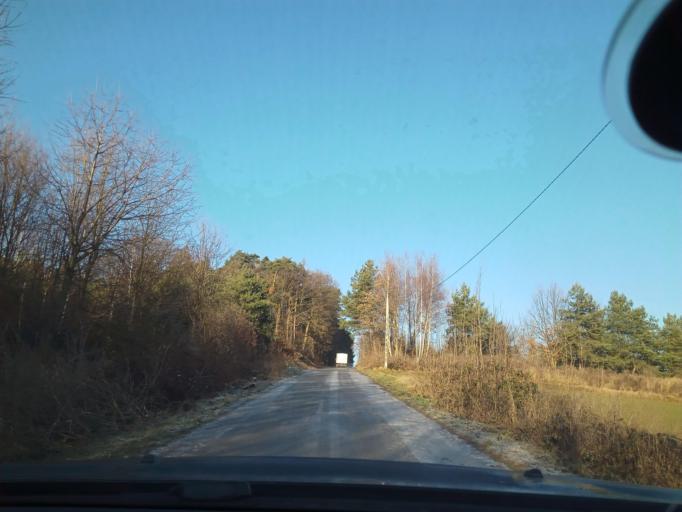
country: PL
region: Lesser Poland Voivodeship
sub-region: Powiat krakowski
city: Michalowice
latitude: 50.1955
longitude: 20.0188
